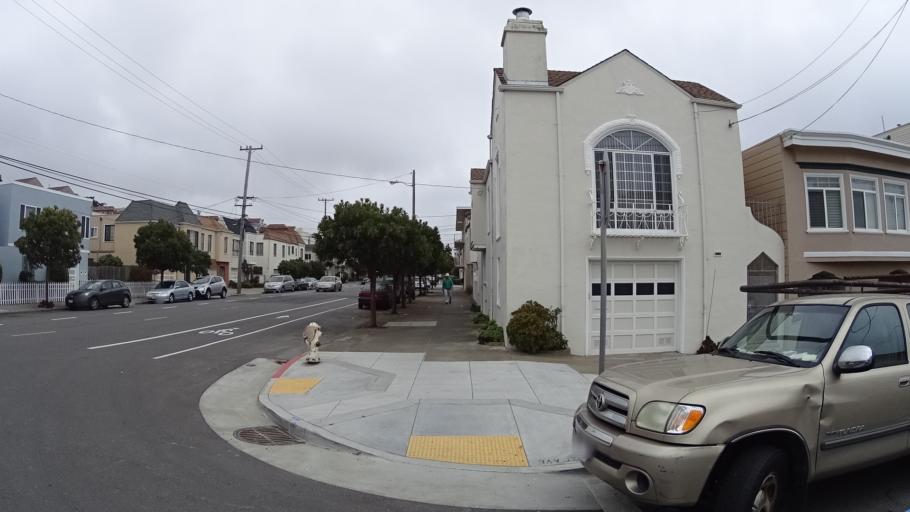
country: US
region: California
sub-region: San Francisco County
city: San Francisco
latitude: 37.7741
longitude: -122.4908
